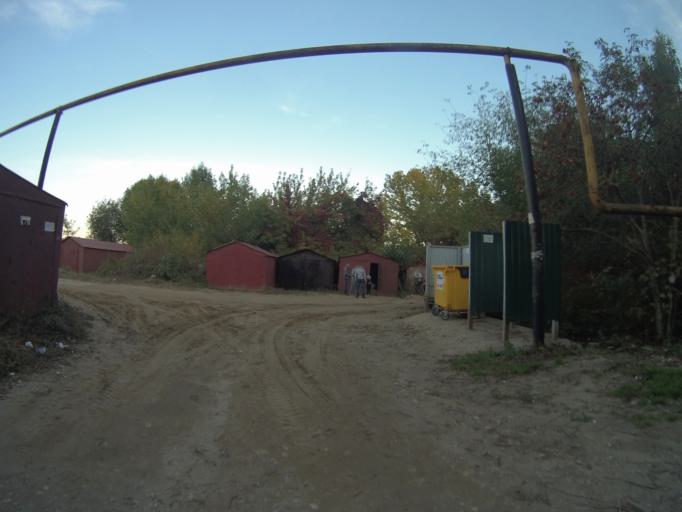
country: RU
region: Vladimir
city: Vladimir
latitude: 56.1147
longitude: 40.3786
